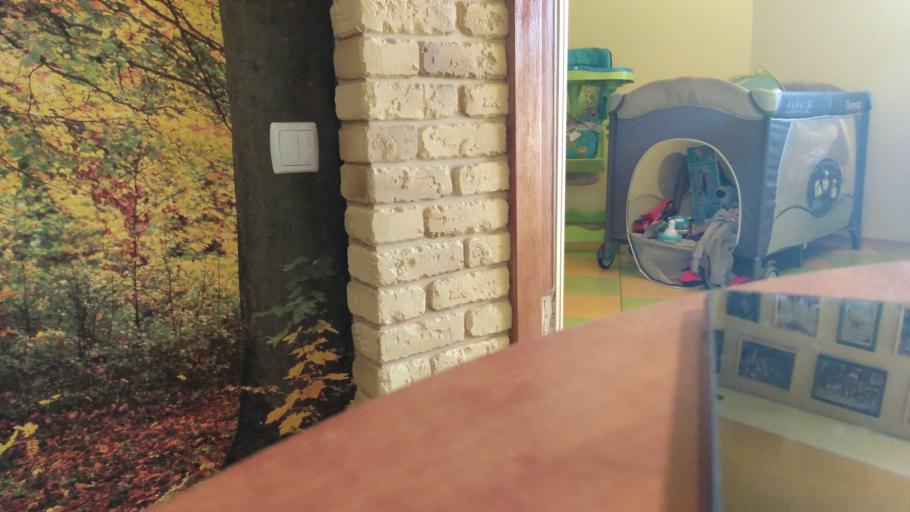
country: RU
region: Tverskaya
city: Bologoye
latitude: 57.9221
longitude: 34.2160
